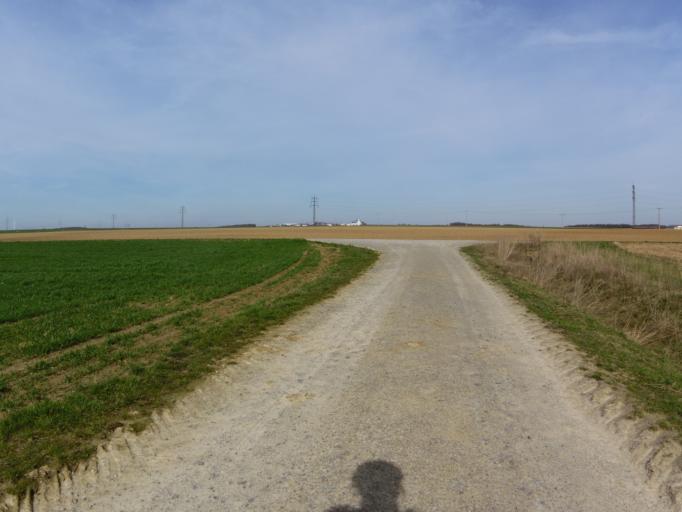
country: DE
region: Bavaria
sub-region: Regierungsbezirk Unterfranken
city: Biebelried
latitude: 49.7517
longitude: 10.0768
